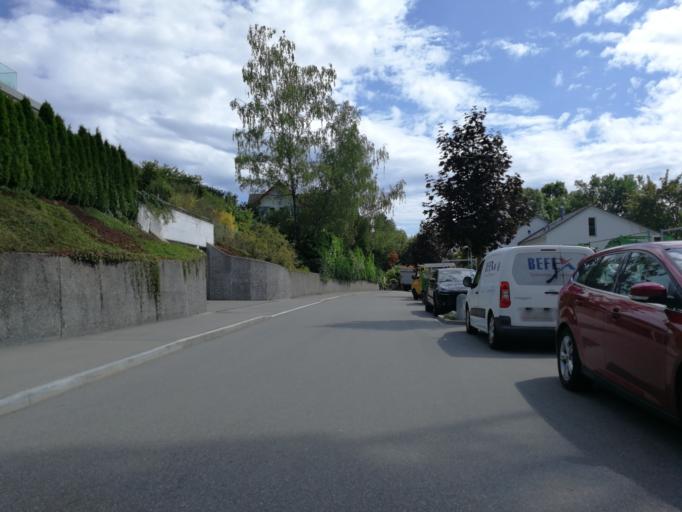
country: CH
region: Zurich
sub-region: Bezirk Meilen
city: Feldmeilen
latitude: 47.2842
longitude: 8.6203
